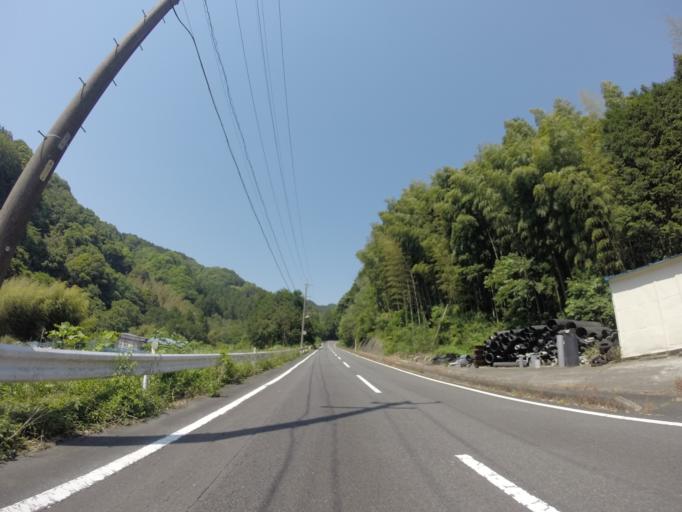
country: JP
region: Shizuoka
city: Fujinomiya
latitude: 35.1464
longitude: 138.5623
